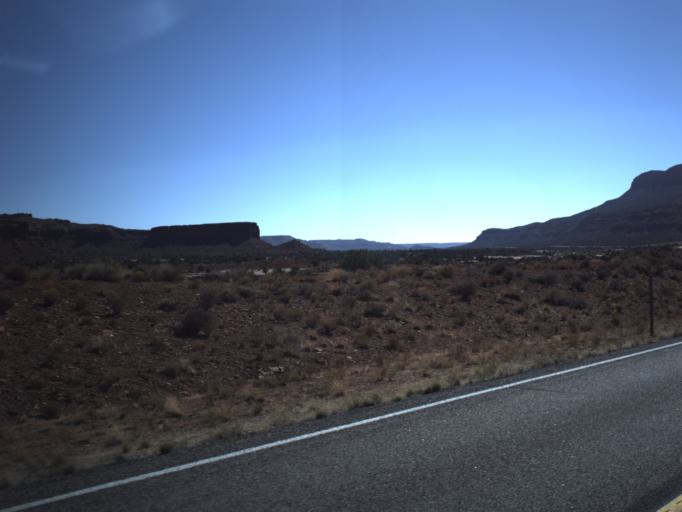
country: US
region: Utah
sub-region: San Juan County
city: Blanding
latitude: 37.6979
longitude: -110.2313
